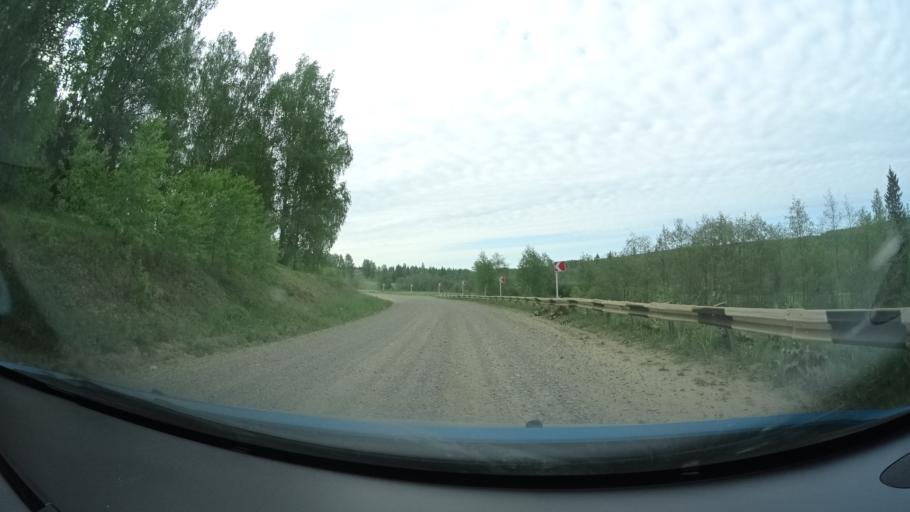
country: RU
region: Perm
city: Kuyeda
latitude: 56.6520
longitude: 55.6952
